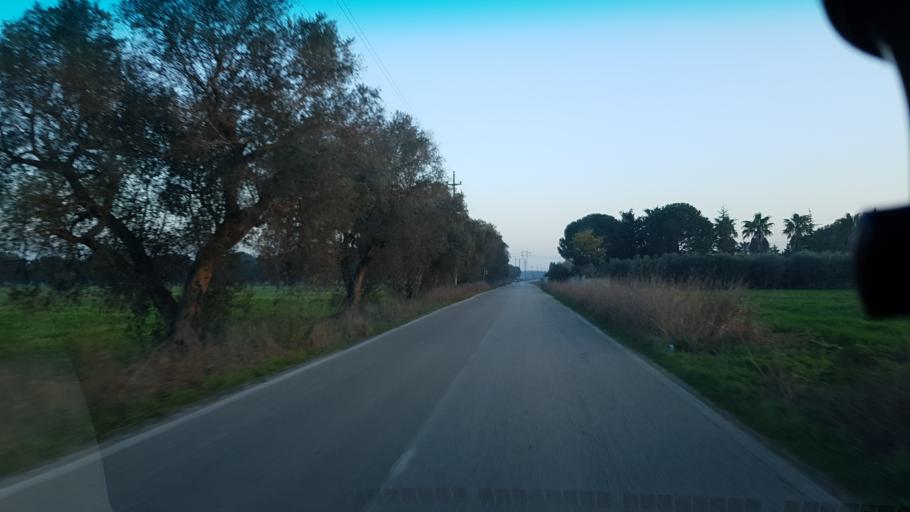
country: IT
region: Apulia
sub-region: Provincia di Brindisi
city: Mesagne
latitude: 40.5911
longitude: 17.7973
